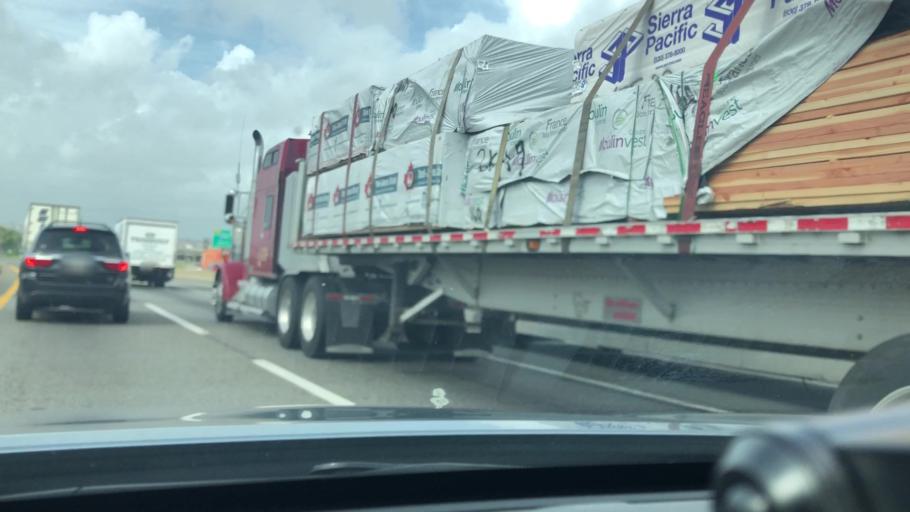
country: US
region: New Jersey
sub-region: Essex County
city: Newark
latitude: 40.7097
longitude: -74.1502
